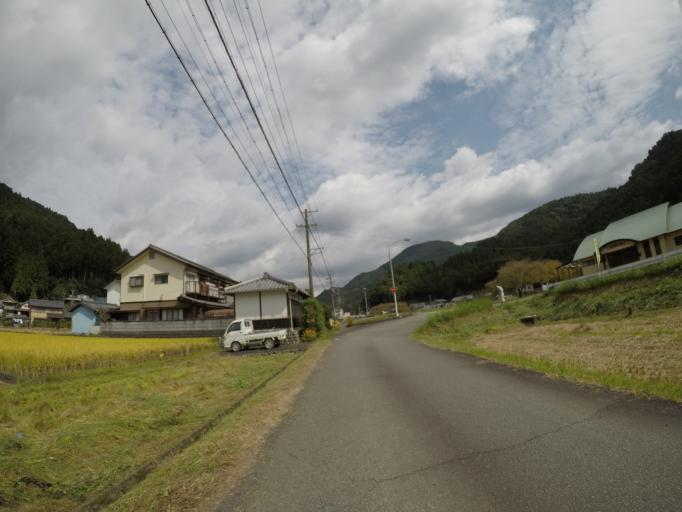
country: JP
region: Shizuoka
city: Kanaya
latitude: 34.8821
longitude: 138.1436
